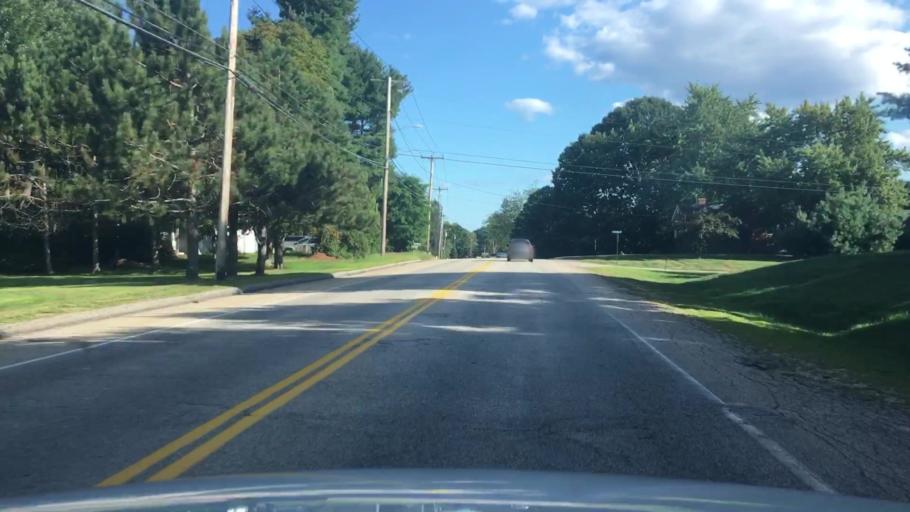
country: US
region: Maine
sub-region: Cumberland County
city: Scarborough
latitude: 43.5727
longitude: -70.3179
